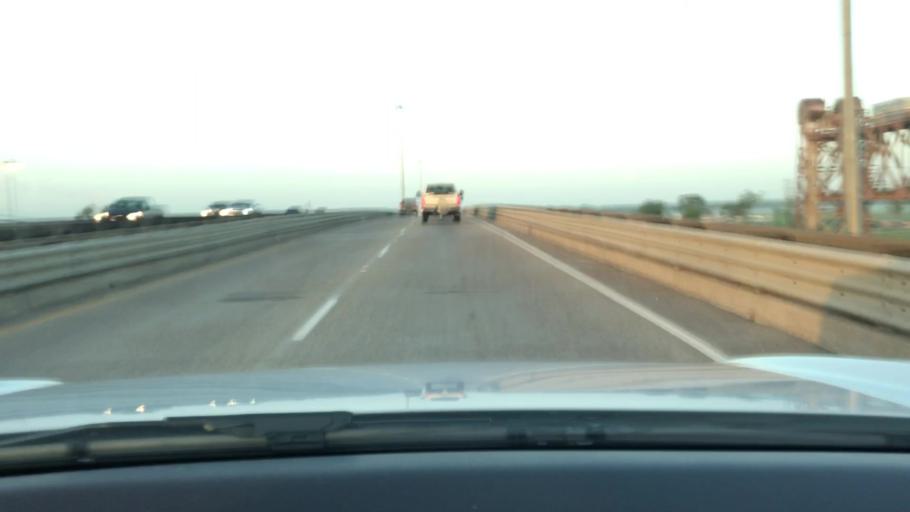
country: US
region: Louisiana
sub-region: West Baton Rouge Parish
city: Port Allen
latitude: 30.4333
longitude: -91.2107
